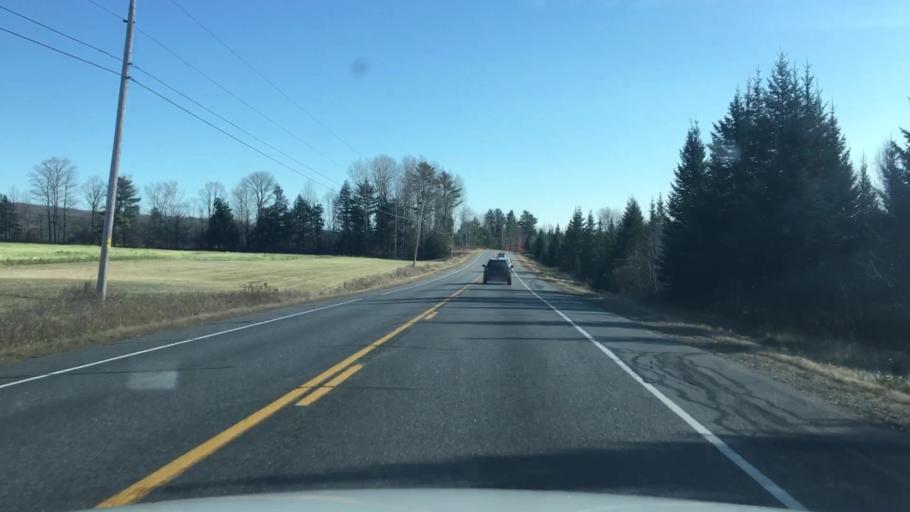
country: US
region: Maine
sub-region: Knox County
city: Washington
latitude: 44.2378
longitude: -69.3582
